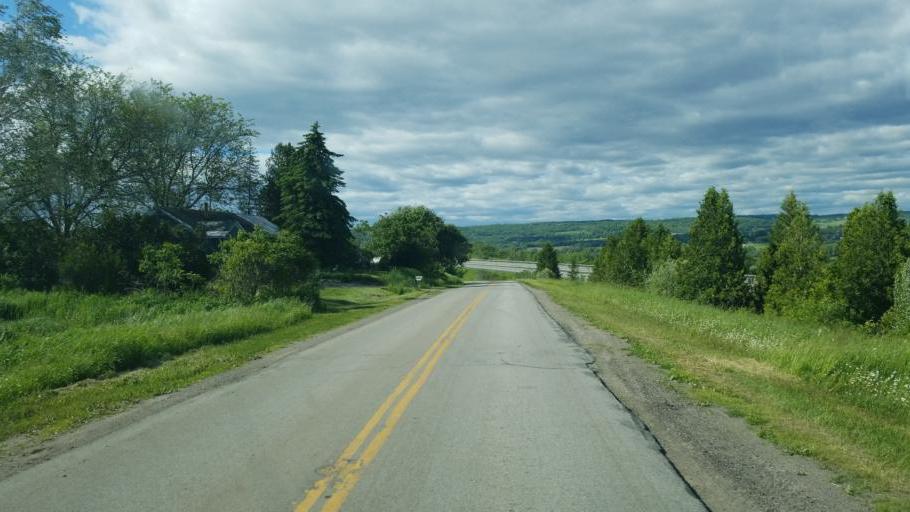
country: US
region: New York
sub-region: Montgomery County
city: Fort Plain
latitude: 42.9541
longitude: -74.6349
